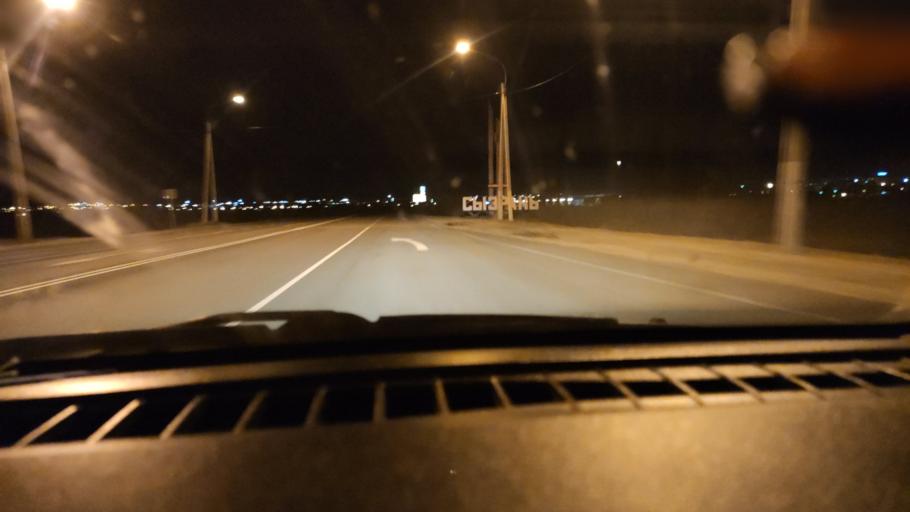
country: RU
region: Samara
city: Syzran'
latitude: 53.2064
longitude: 48.5086
